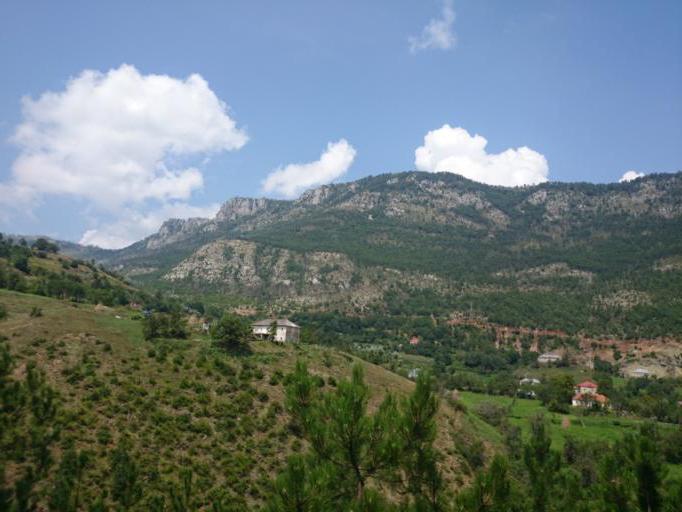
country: AL
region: Diber
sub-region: Rrethi i Dibres
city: Fushe-Lure
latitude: 41.8327
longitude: 20.1842
